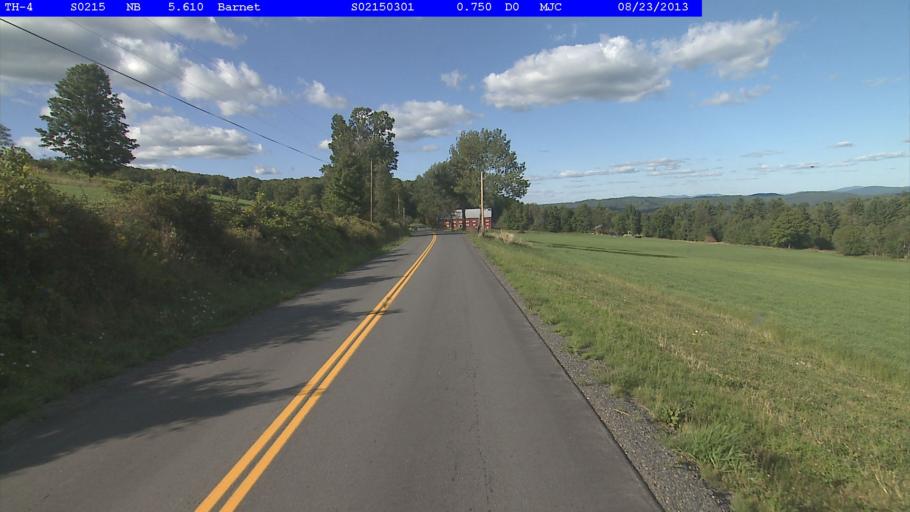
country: US
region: New Hampshire
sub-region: Grafton County
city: Woodsville
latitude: 44.2848
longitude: -72.1706
